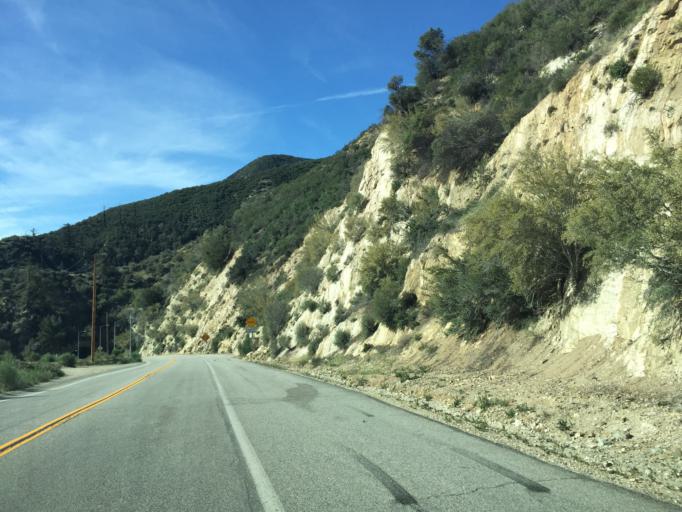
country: US
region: California
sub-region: San Bernardino County
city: San Antonio Heights
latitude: 34.2064
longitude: -117.6760
